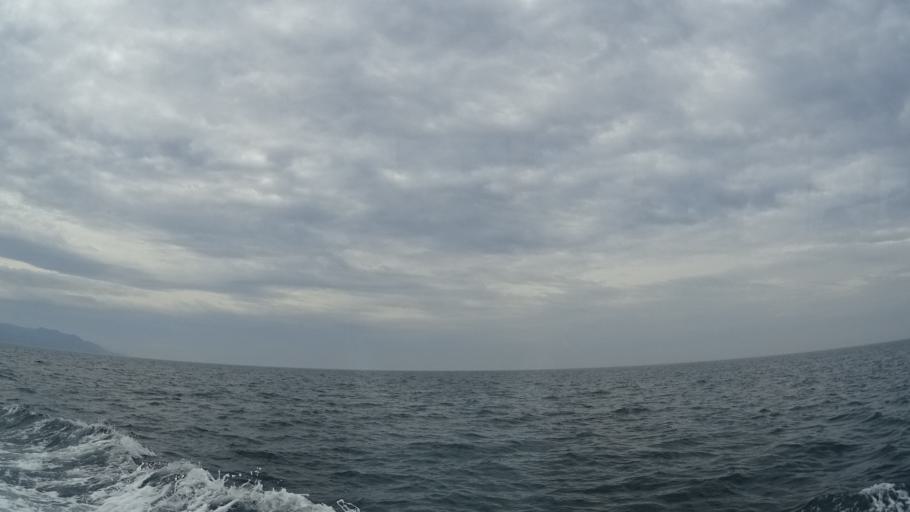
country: JP
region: Fukui
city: Mikuni
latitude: 36.2457
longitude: 136.1199
